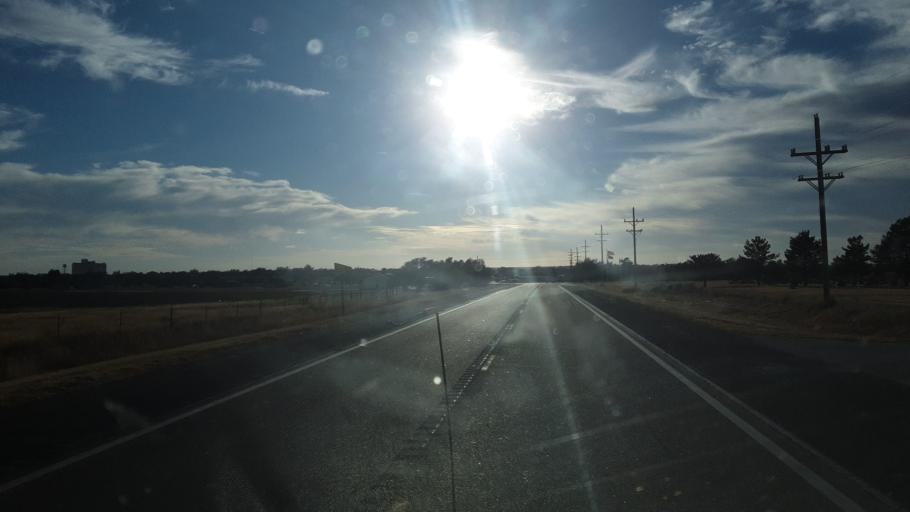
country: US
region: Kansas
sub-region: Kearny County
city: Lakin
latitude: 37.9522
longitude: -101.2453
